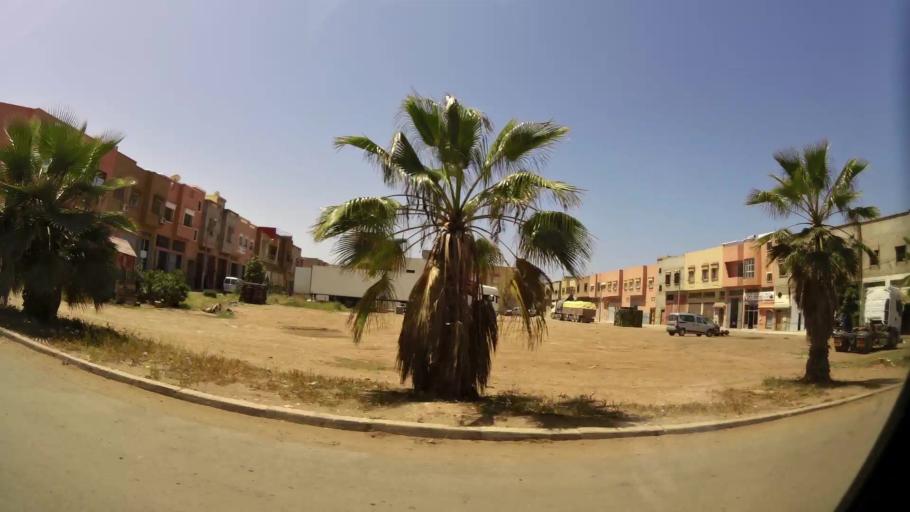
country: MA
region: Souss-Massa-Draa
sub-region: Inezgane-Ait Mellou
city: Inezgane
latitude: 30.3309
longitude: -9.4919
